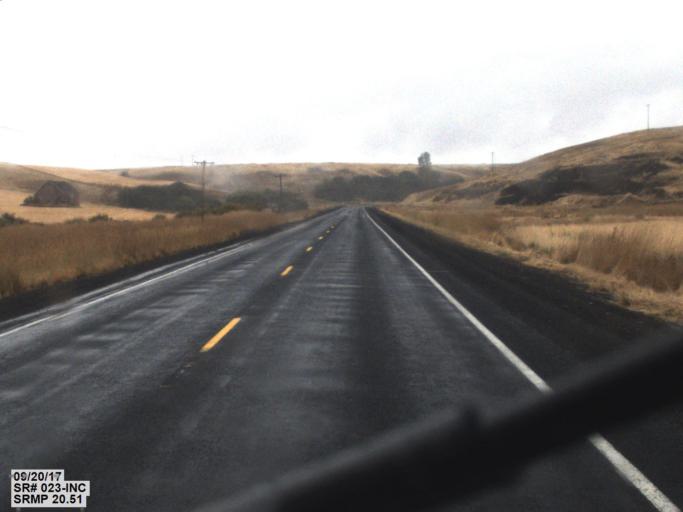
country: US
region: Washington
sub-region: Spokane County
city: Cheney
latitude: 47.1131
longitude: -117.7004
